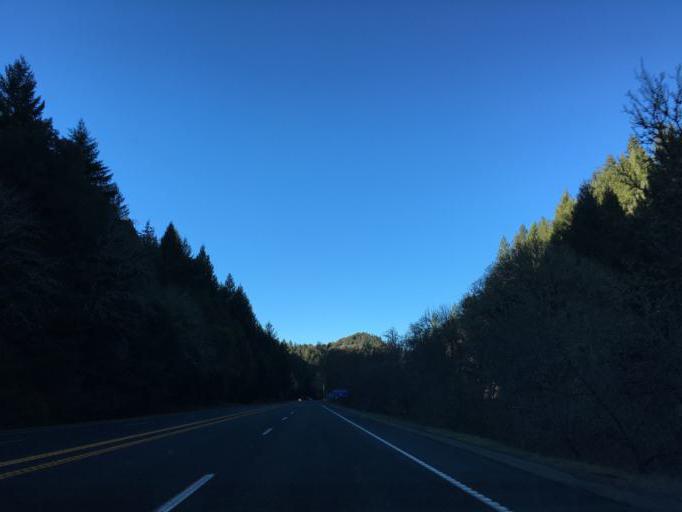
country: US
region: California
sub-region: Mendocino County
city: Laytonville
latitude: 39.5847
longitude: -123.4462
